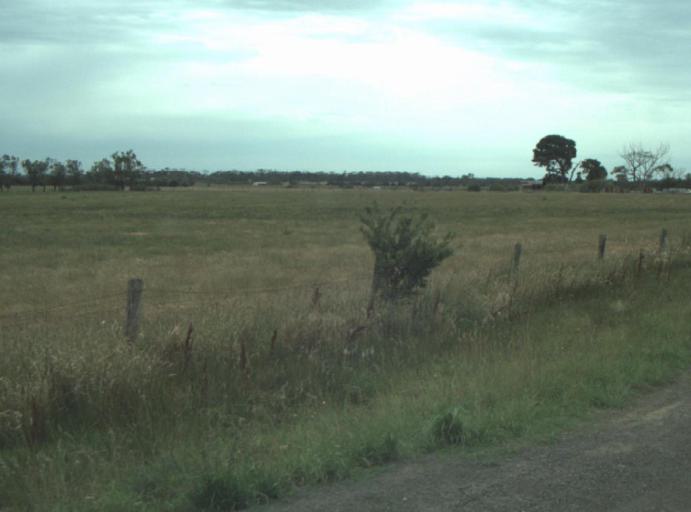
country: AU
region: Victoria
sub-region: Greater Geelong
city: Leopold
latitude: -38.2032
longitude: 144.4523
